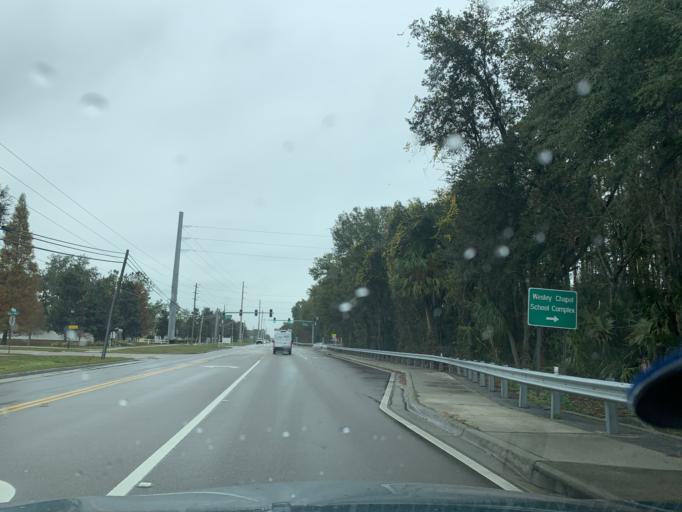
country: US
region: Florida
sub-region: Pasco County
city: Wesley Chapel
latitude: 28.2560
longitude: -82.3201
